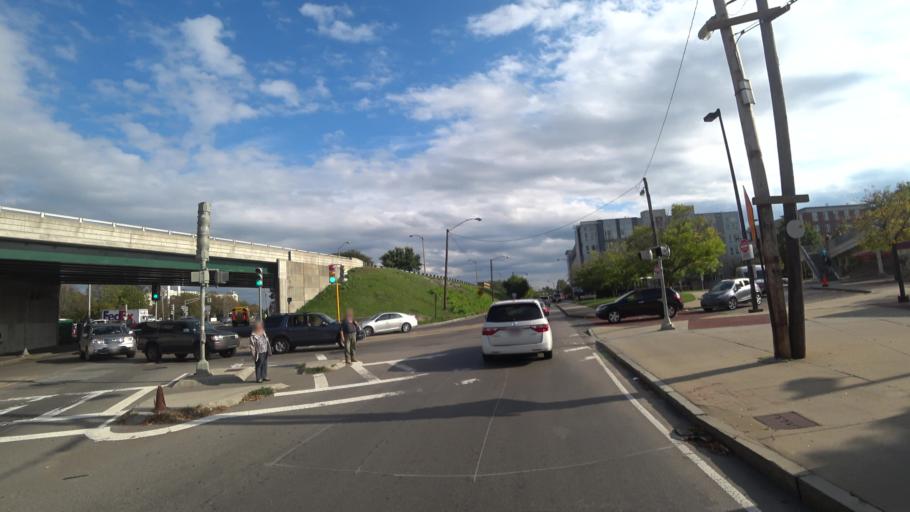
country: US
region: Massachusetts
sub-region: Suffolk County
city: South Boston
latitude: 42.3210
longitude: -71.0514
